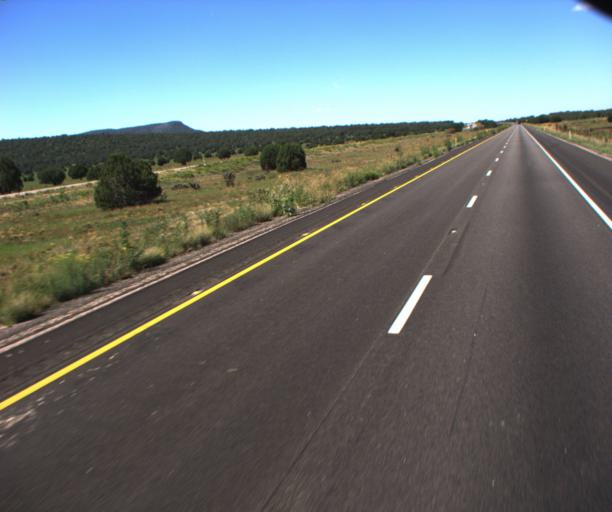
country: US
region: Arizona
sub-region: Mohave County
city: Peach Springs
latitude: 35.2297
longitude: -113.2260
